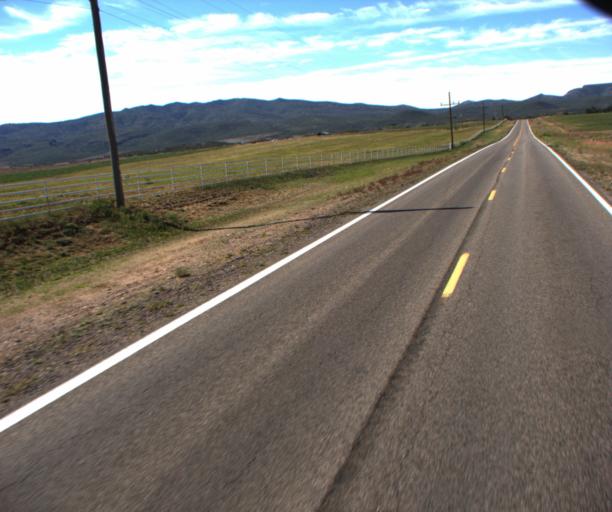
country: US
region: Arizona
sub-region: Yavapai County
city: Congress
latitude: 34.2911
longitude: -112.7230
